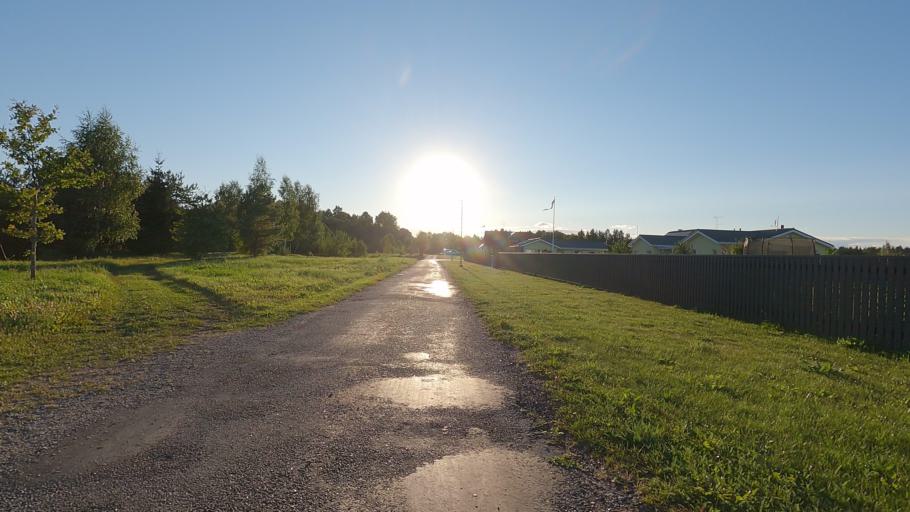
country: EE
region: Raplamaa
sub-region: Rapla vald
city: Rapla
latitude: 59.0025
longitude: 24.7817
